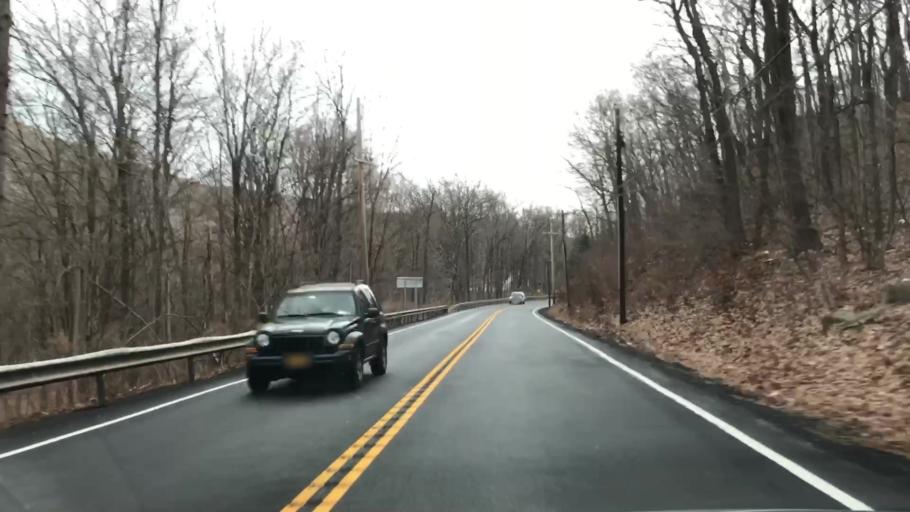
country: US
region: New York
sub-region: Rockland County
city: Wesley Hills
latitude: 41.1735
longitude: -74.0825
